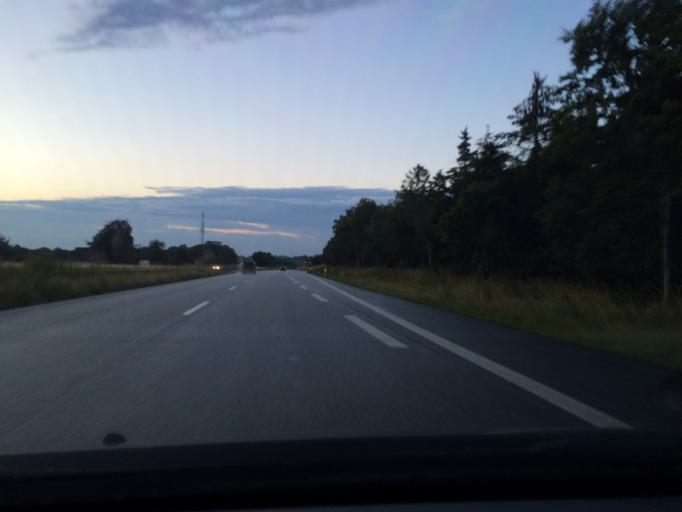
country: DK
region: Zealand
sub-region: Koge Kommune
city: Ejby
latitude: 55.4595
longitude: 12.1215
